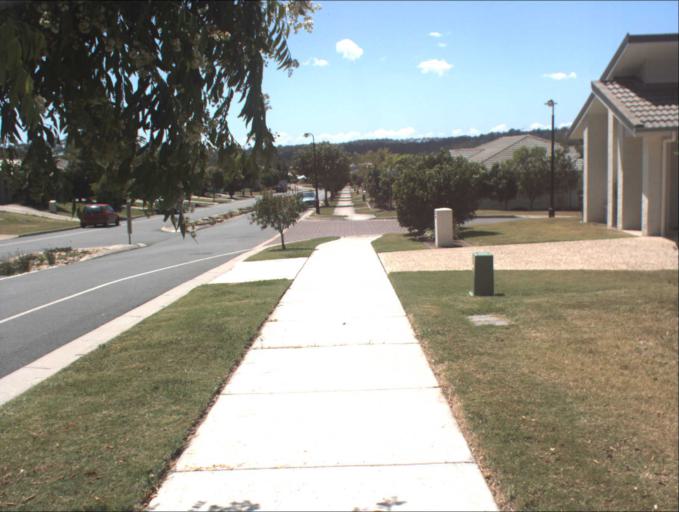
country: AU
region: Queensland
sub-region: Logan
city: Windaroo
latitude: -27.7508
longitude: 153.1819
